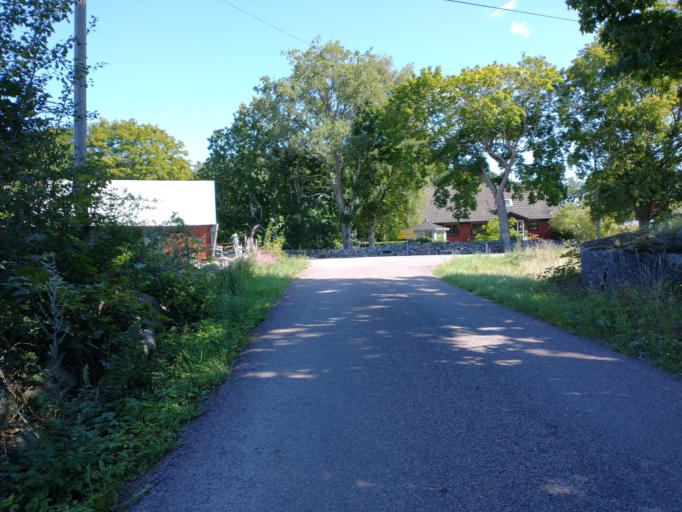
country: SE
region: Kalmar
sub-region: Kalmar Kommun
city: Lindsdal
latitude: 56.7963
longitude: 16.2674
